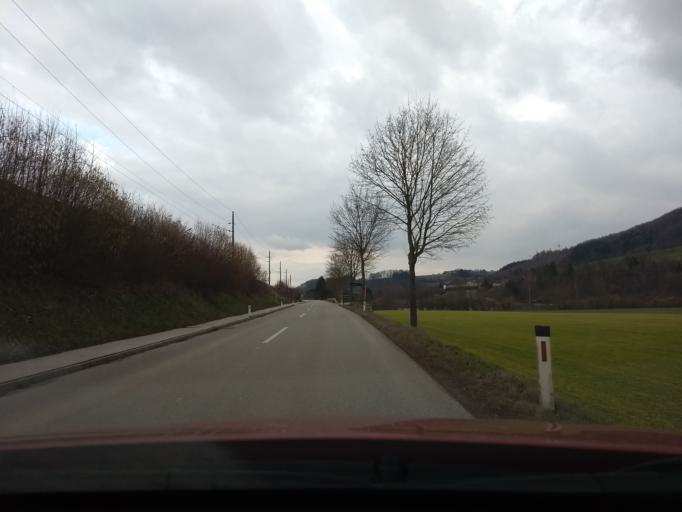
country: AT
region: Upper Austria
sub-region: Politischer Bezirk Steyr-Land
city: Garsten
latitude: 48.0023
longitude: 14.4046
